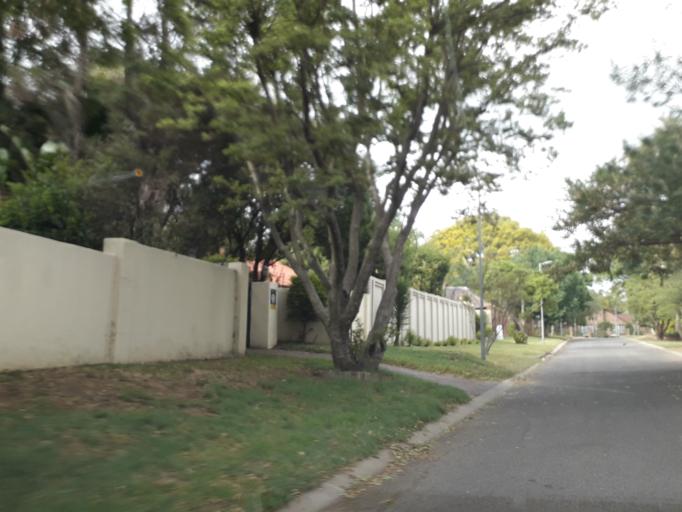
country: ZA
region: Gauteng
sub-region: City of Johannesburg Metropolitan Municipality
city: Roodepoort
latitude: -26.1048
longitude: 27.9577
